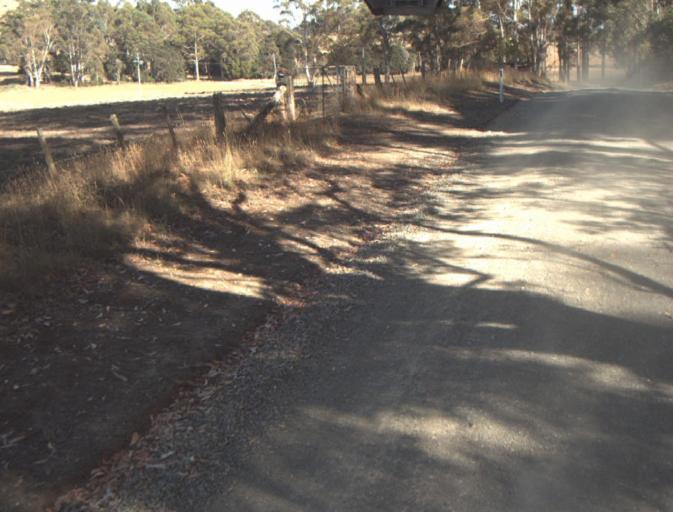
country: AU
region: Tasmania
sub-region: Dorset
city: Bridport
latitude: -41.1588
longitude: 147.2369
